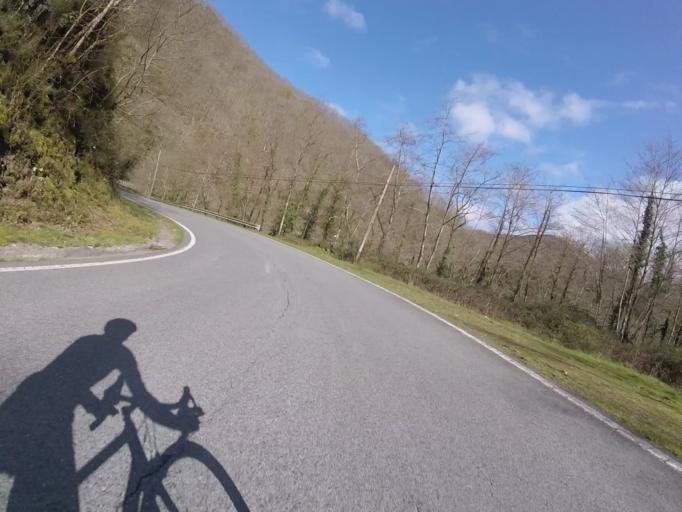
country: ES
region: Navarre
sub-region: Provincia de Navarra
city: Goizueta
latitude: 43.1359
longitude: -1.8500
